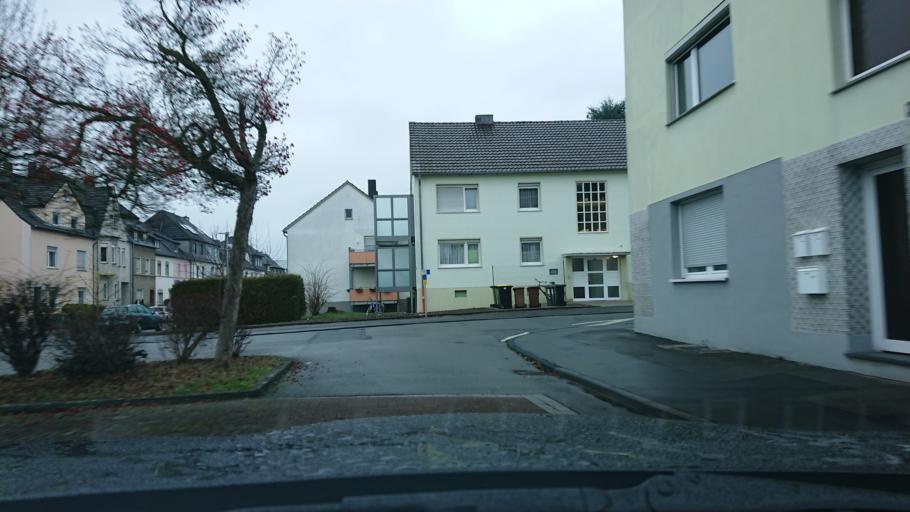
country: DE
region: North Rhine-Westphalia
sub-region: Regierungsbezirk Koln
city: Siegburg
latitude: 50.8084
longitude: 7.1900
